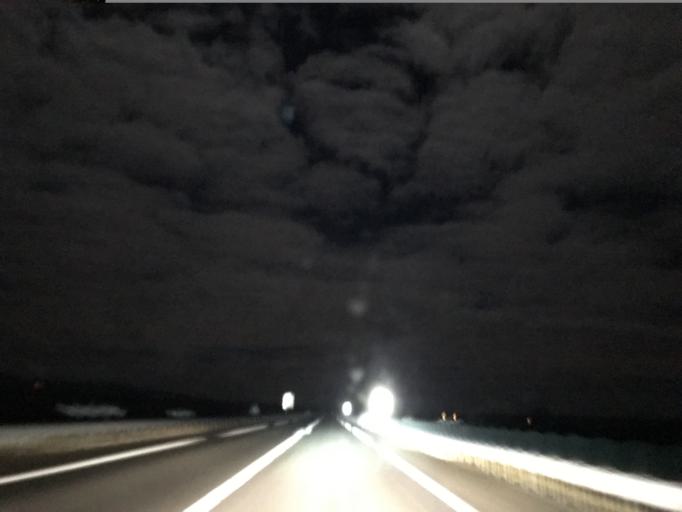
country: FR
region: Auvergne
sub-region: Departement de l'Allier
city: Saint-Yorre
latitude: 46.0527
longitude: 3.4514
